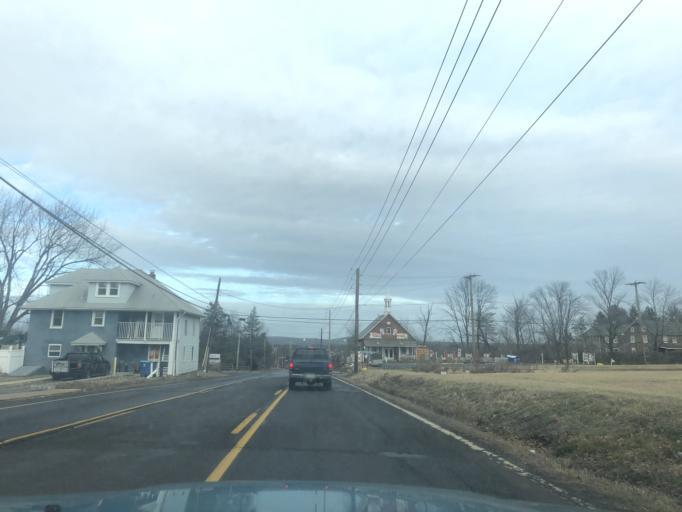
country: US
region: Pennsylvania
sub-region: Montgomery County
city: Telford
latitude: 40.3276
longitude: -75.3030
